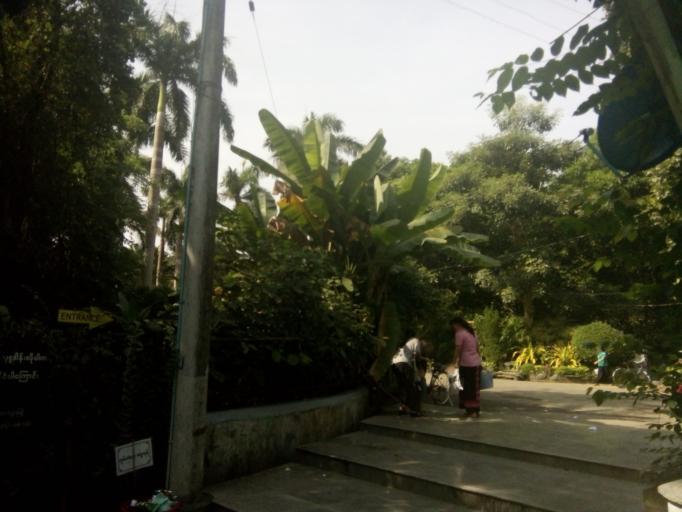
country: MM
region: Yangon
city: Yangon
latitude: 16.7945
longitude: 96.1591
